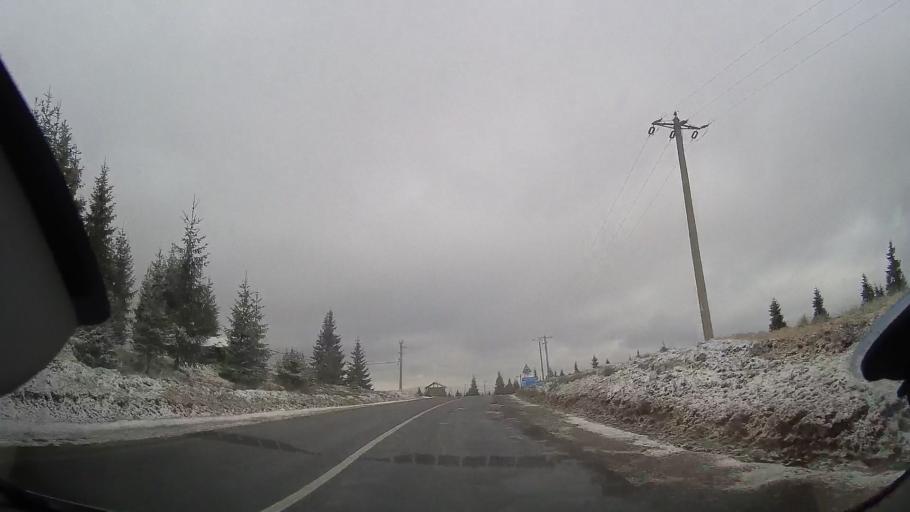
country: RO
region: Cluj
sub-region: Comuna Belis
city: Belis
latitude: 46.6945
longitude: 23.0388
